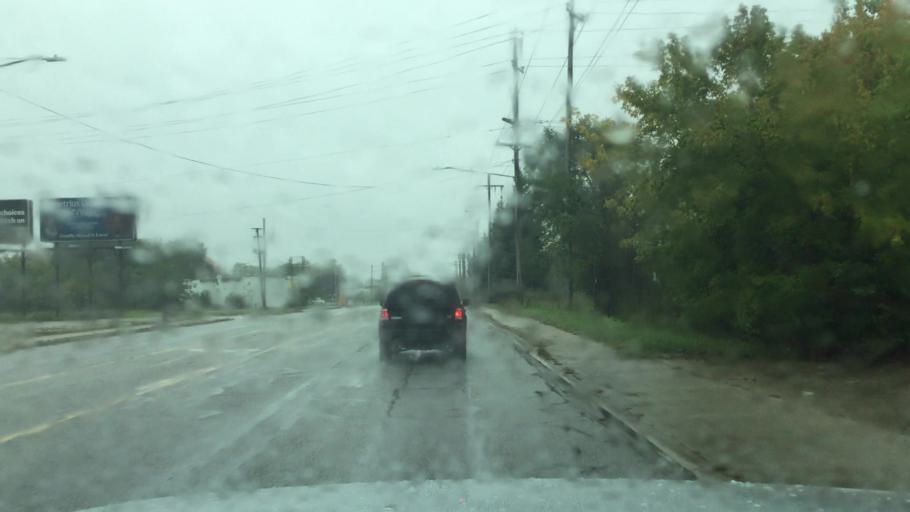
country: US
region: Michigan
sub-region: Saginaw County
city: Buena Vista
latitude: 43.4120
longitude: -83.9198
